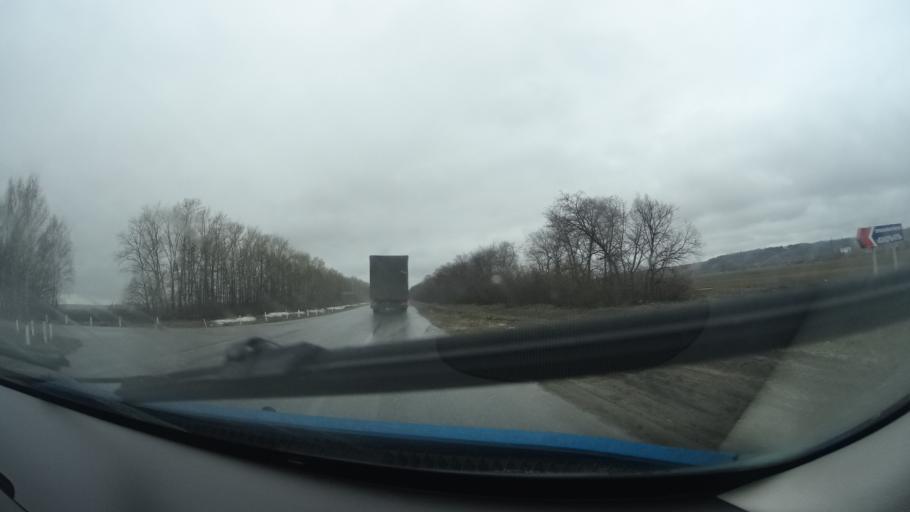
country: RU
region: Bashkortostan
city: Kandry
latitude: 54.5339
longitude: 54.1021
